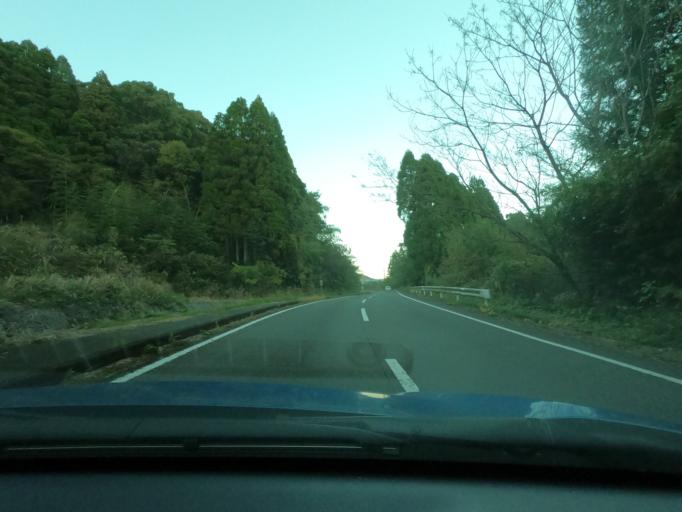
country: JP
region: Kagoshima
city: Satsumasendai
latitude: 31.8175
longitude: 130.4831
